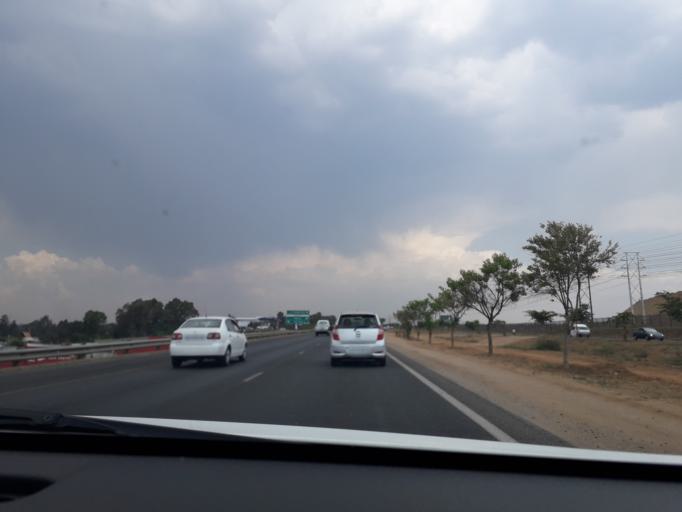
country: ZA
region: Gauteng
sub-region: City of Johannesburg Metropolitan Municipality
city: Midrand
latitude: -26.0297
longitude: 28.1344
